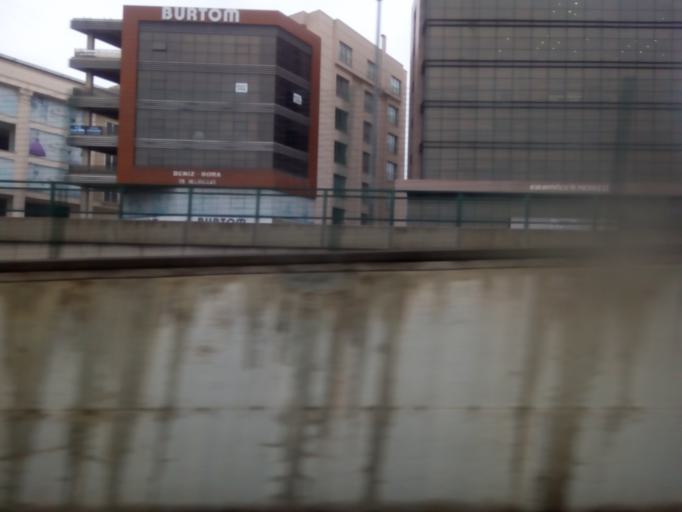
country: TR
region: Bursa
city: Yildirim
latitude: 40.2310
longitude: 28.9841
